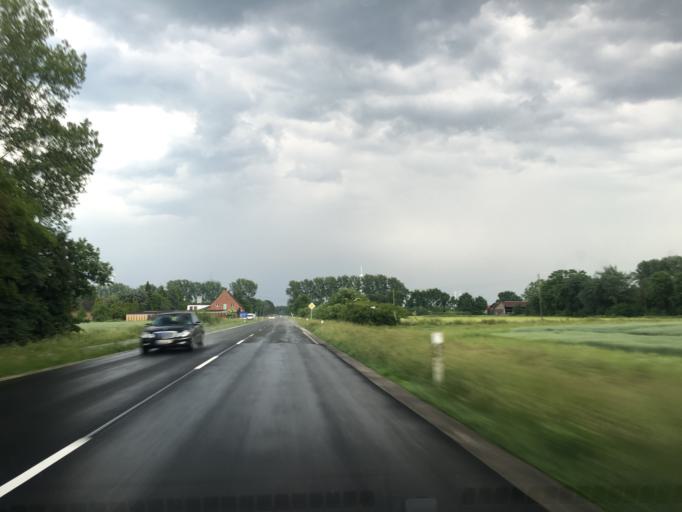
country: DE
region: North Rhine-Westphalia
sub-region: Regierungsbezirk Munster
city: Altenberge
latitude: 52.0865
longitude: 7.4236
